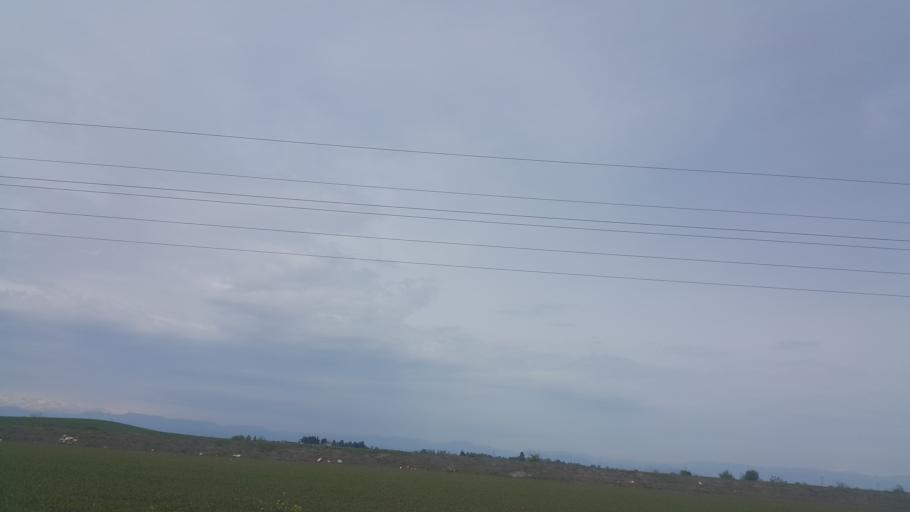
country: TR
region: Adana
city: Ceyhan
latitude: 37.0550
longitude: 35.8637
